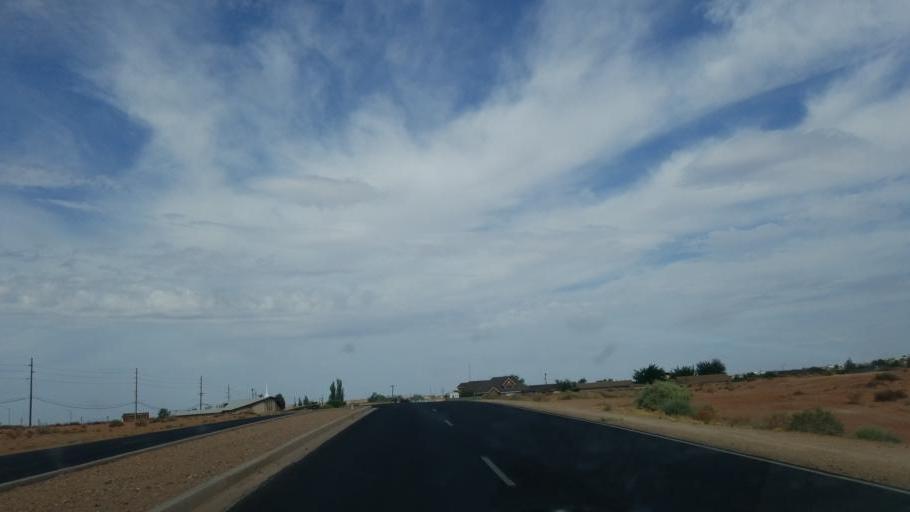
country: US
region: Arizona
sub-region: Navajo County
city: Winslow
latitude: 35.0397
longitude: -110.7219
